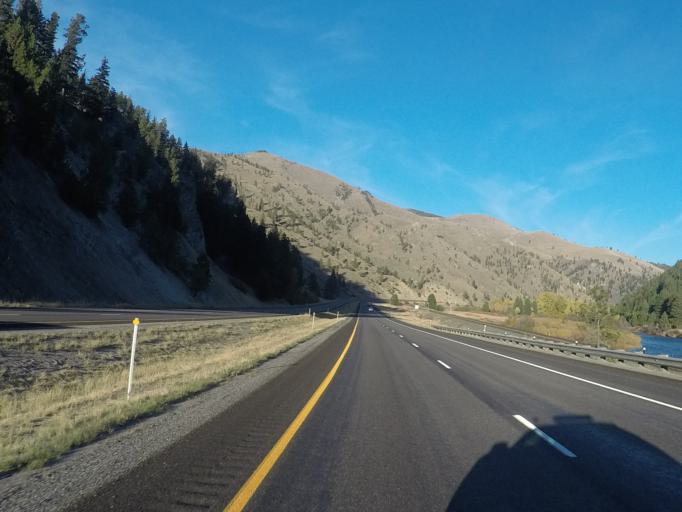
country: US
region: Montana
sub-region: Missoula County
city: Clinton
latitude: 46.6972
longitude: -113.4808
